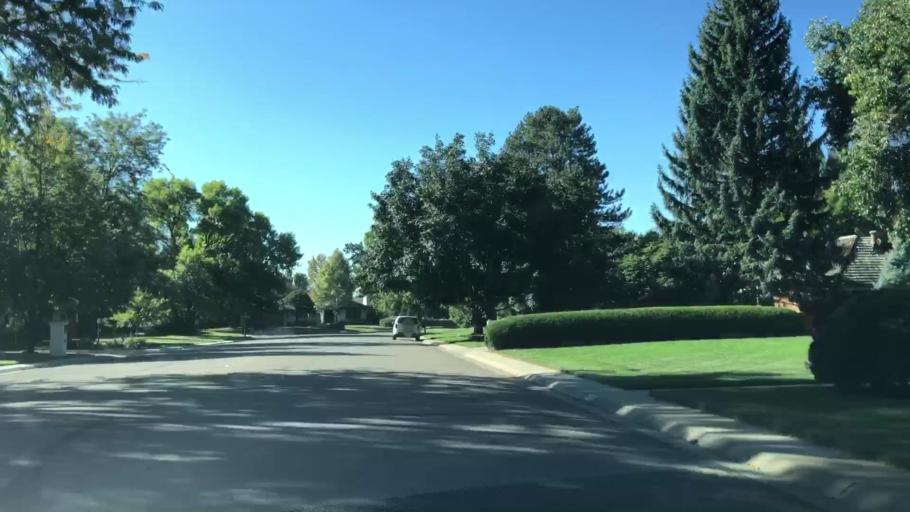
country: US
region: Colorado
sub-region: Larimer County
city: Fort Collins
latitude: 40.5542
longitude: -105.0539
